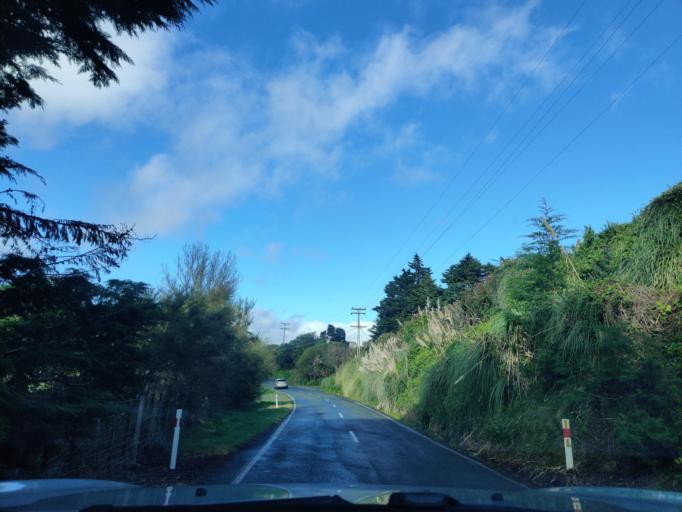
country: NZ
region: Hawke's Bay
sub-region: Hastings District
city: Hastings
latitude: -39.6857
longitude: 176.8984
